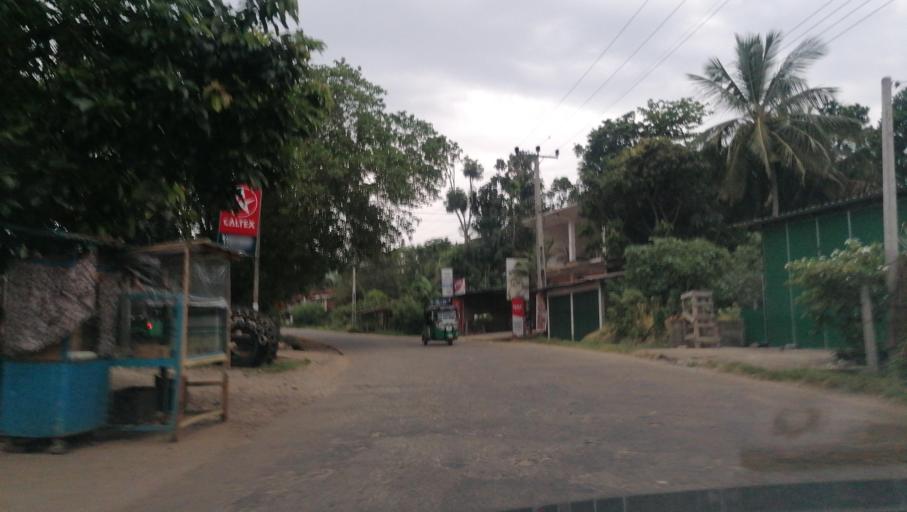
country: LK
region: Central
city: Kandy
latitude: 7.2137
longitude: 80.7811
